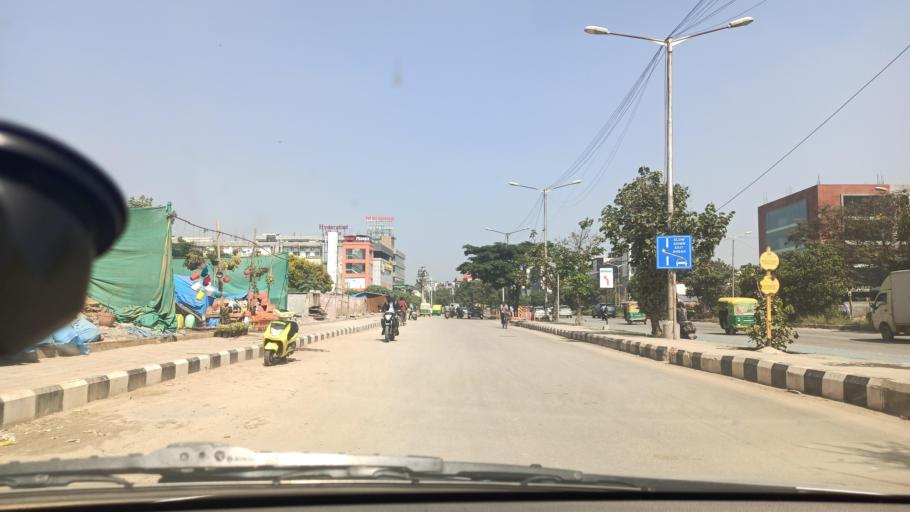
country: IN
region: Karnataka
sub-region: Bangalore Urban
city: Bangalore
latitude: 12.9464
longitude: 77.6984
